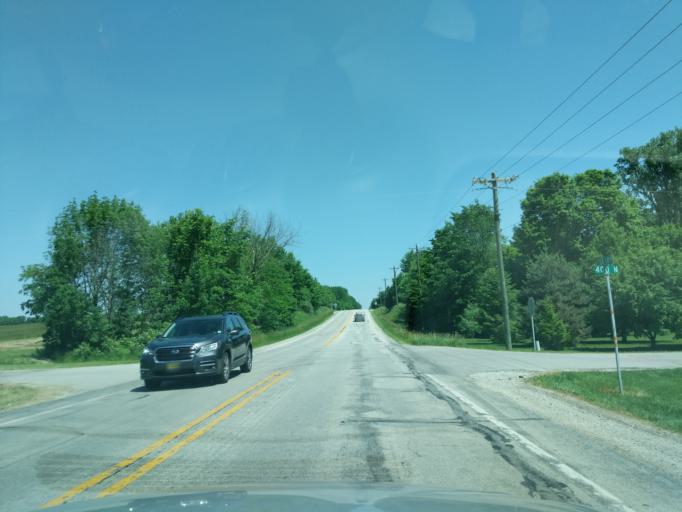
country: US
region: Indiana
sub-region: Whitley County
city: Tri-Lakes
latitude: 41.2215
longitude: -85.4919
